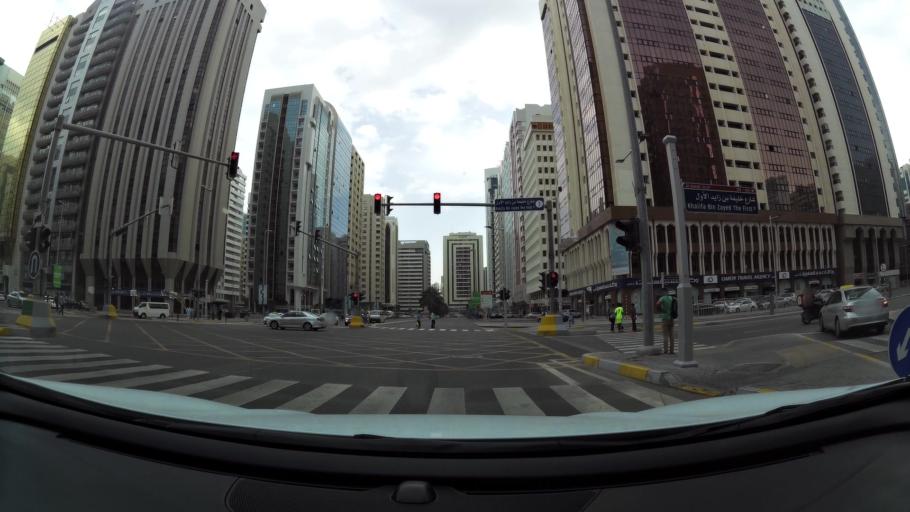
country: AE
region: Abu Dhabi
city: Abu Dhabi
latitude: 24.4897
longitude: 54.3577
